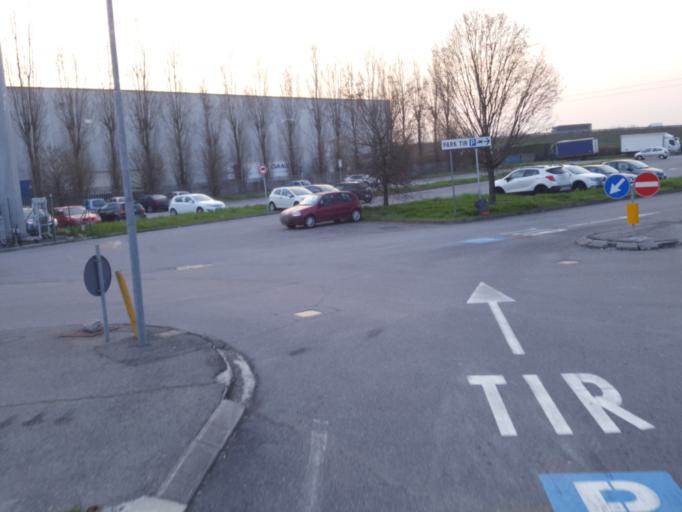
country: IT
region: Lombardy
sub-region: Citta metropolitana di Milano
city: Liscate
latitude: 45.4746
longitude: 9.4234
